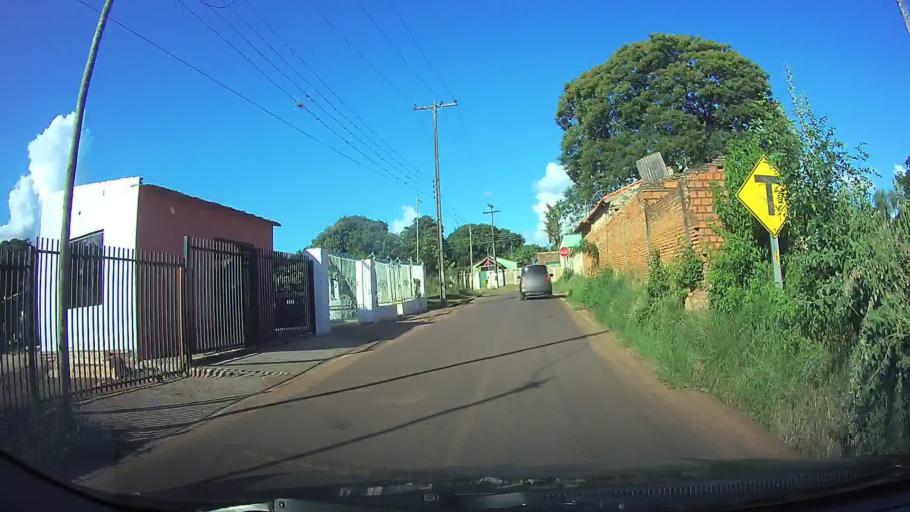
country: PY
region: Central
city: Aregua
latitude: -25.3398
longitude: -57.3849
